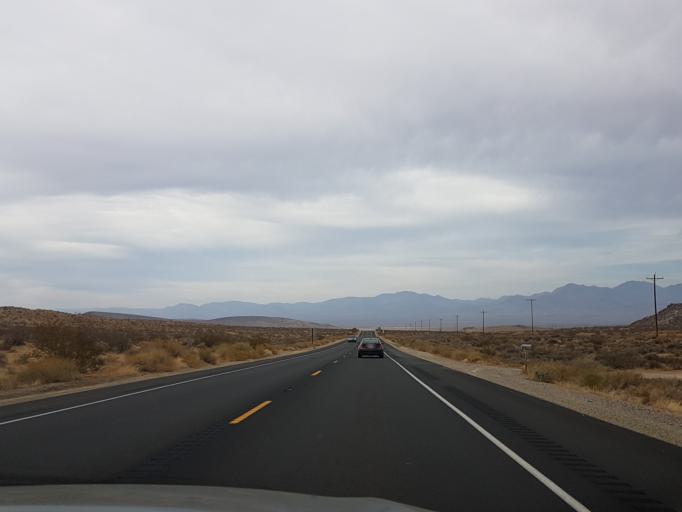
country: US
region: California
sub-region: Kern County
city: Ridgecrest
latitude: 35.5462
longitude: -117.6983
